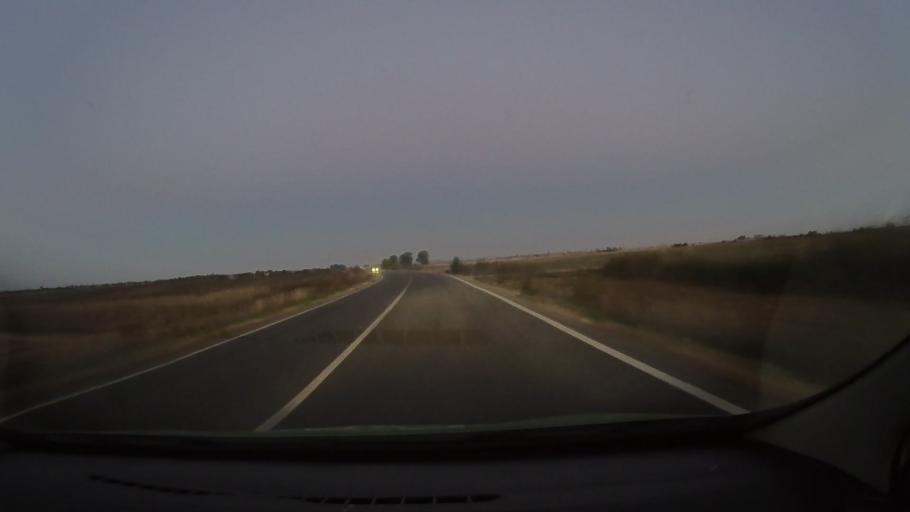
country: RO
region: Bihor
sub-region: Comuna Simian
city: Simian
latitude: 47.5087
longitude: 22.1009
